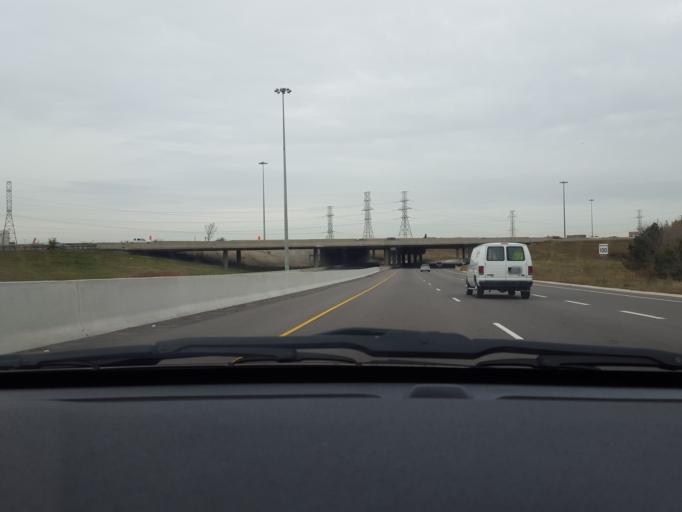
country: CA
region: Ontario
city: Etobicoke
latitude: 43.6752
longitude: -79.5756
